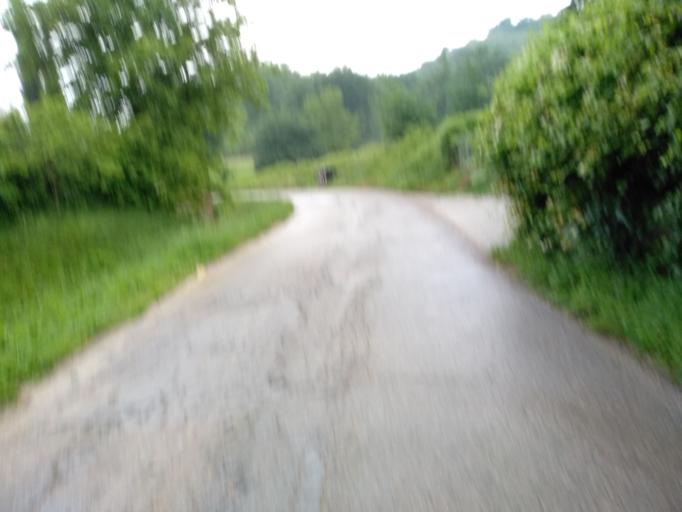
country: IT
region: Tuscany
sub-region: Province of Arezzo
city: Vacchereccia
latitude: 43.5565
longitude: 11.5167
